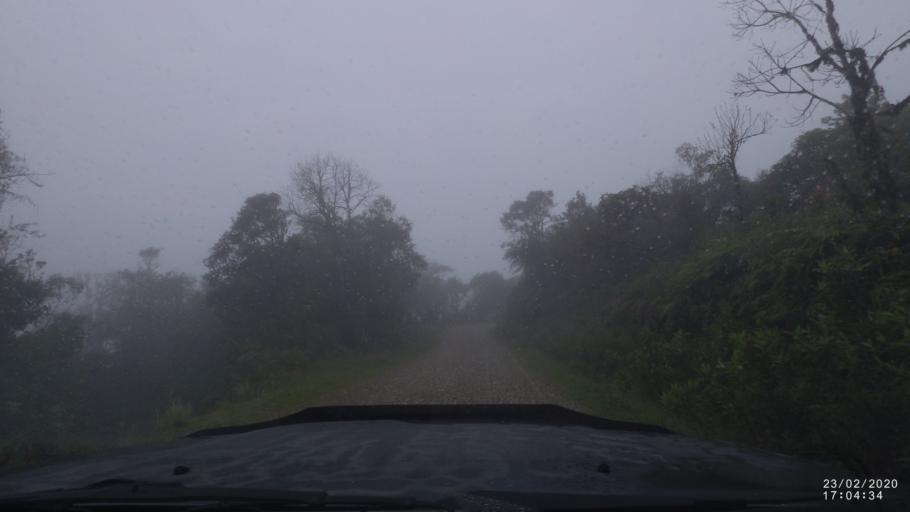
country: BO
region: Cochabamba
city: Colomi
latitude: -17.1247
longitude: -65.9644
